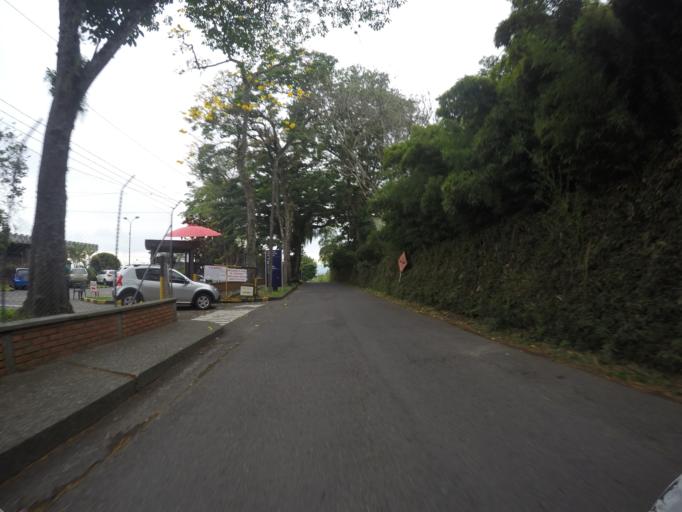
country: CO
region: Risaralda
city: Pereira
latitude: 4.8162
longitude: -75.7368
